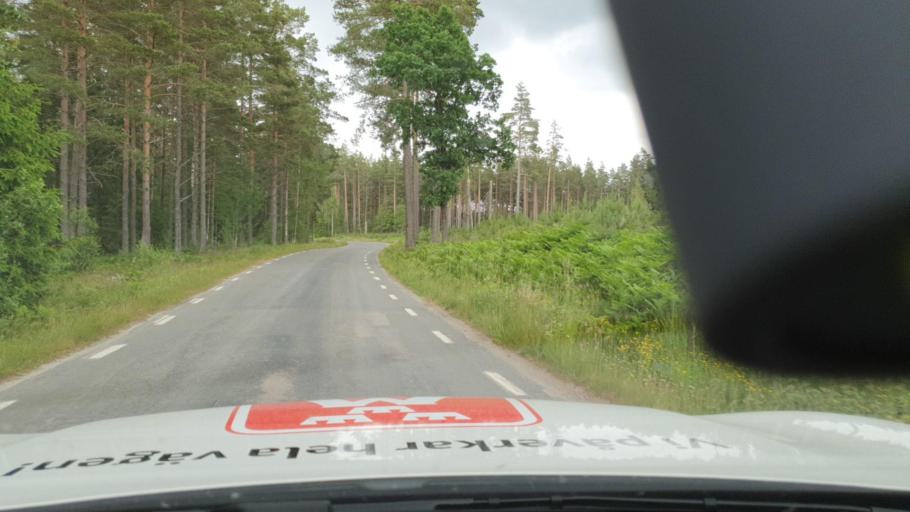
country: SE
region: Vaestra Goetaland
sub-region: Tidaholms Kommun
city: Olofstorp
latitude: 58.1760
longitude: 14.1488
